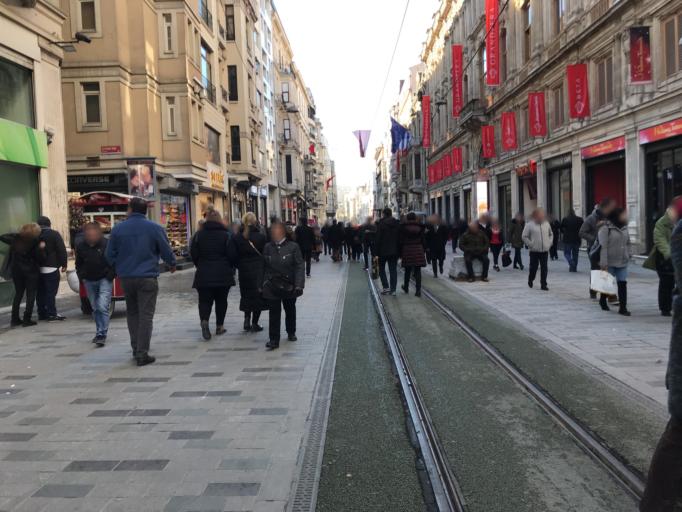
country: TR
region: Istanbul
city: Eminoenue
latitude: 41.0347
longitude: 28.9801
